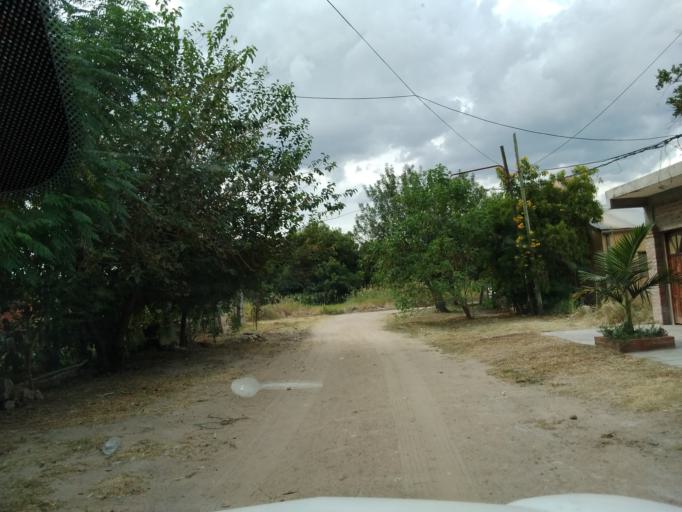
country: AR
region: Corrientes
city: Corrientes
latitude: -27.5212
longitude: -58.7953
